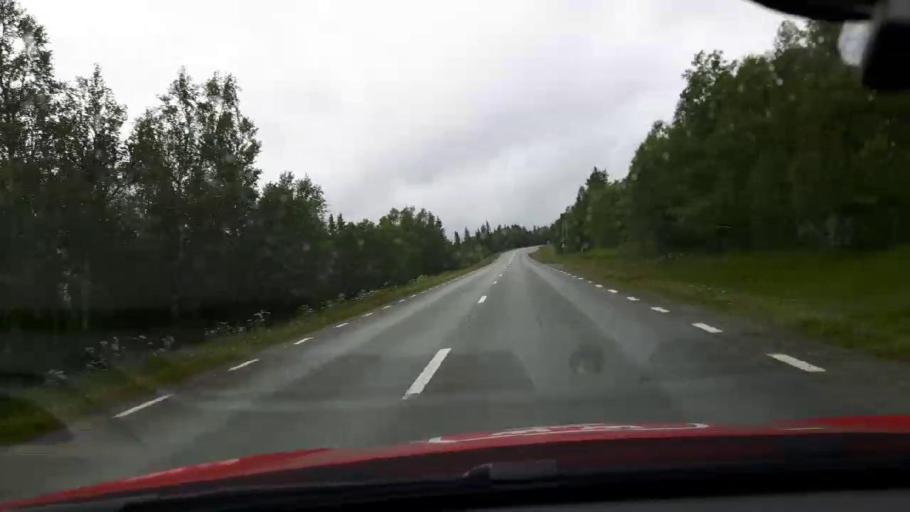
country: NO
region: Nord-Trondelag
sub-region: Meraker
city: Meraker
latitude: 63.2960
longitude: 12.1156
